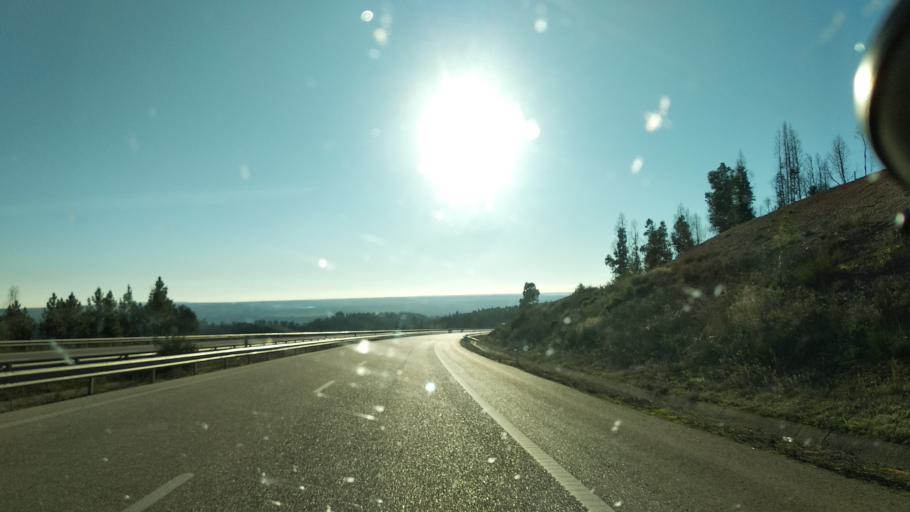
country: PT
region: Santarem
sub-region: Macao
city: Macao
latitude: 39.5039
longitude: -8.0252
